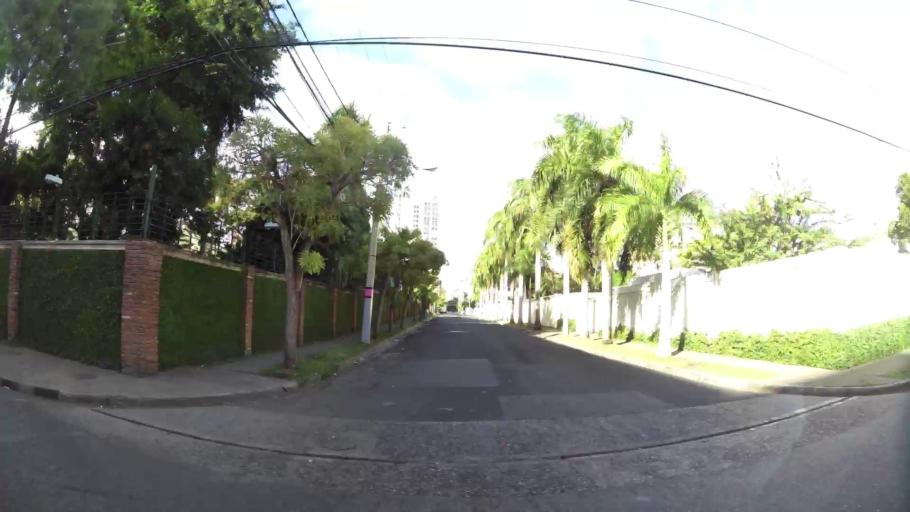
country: DO
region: Nacional
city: La Julia
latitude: 18.4718
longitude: -69.9363
